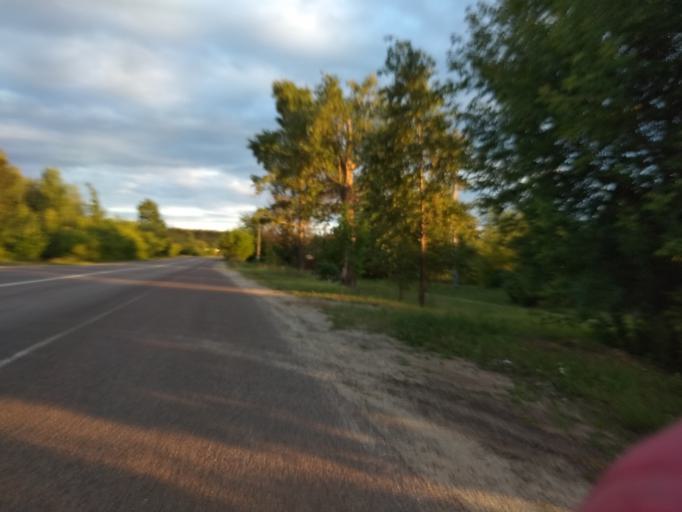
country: RU
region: Moskovskaya
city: Kerva
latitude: 55.5899
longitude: 39.7009
